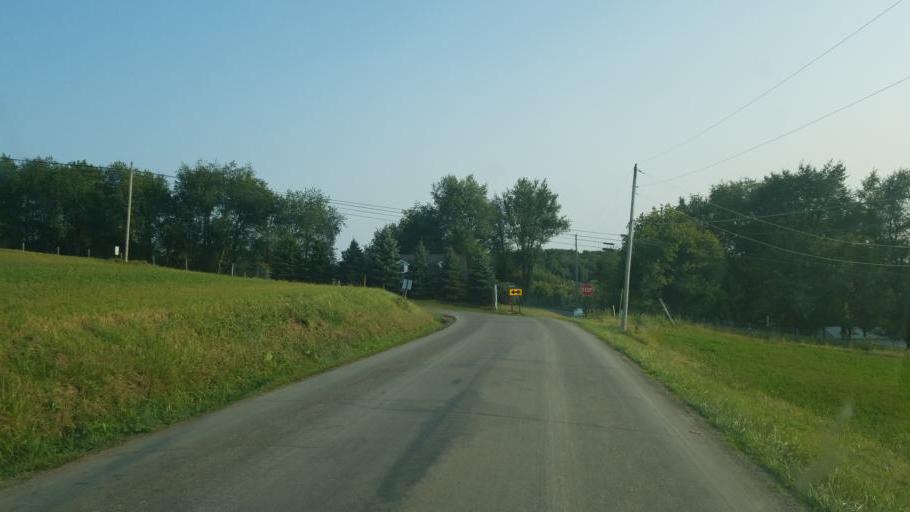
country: US
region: Ohio
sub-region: Wayne County
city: Apple Creek
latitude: 40.6874
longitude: -81.8521
